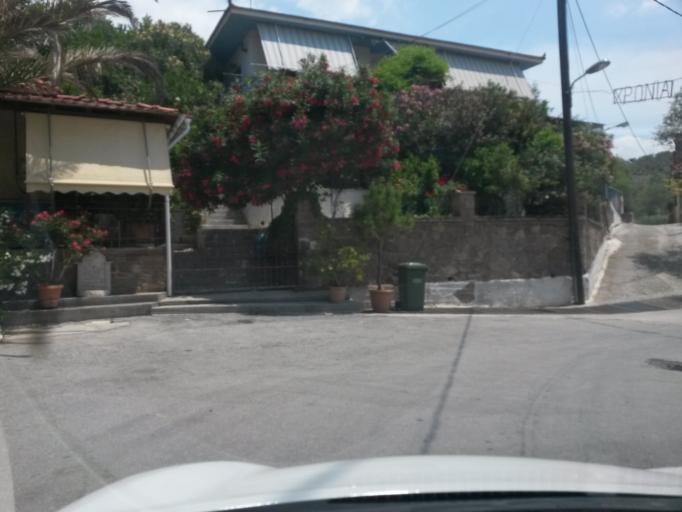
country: GR
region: North Aegean
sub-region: Nomos Lesvou
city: Agiasos
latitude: 39.1836
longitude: 26.4075
